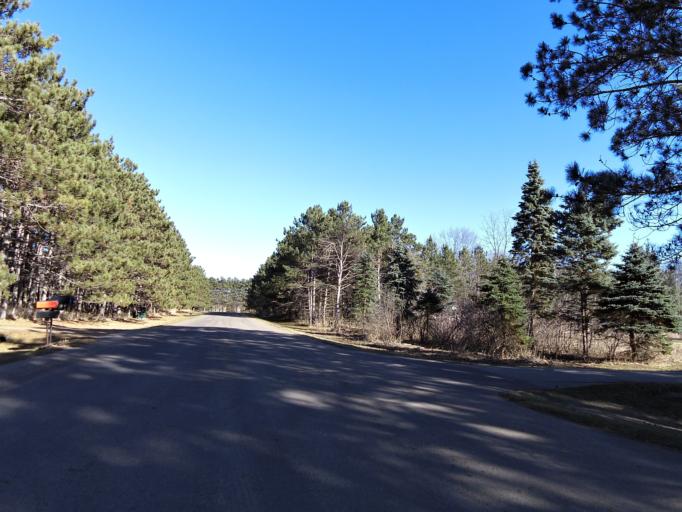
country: US
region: Minnesota
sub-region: Washington County
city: Lake Elmo
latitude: 44.9826
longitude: -92.8248
